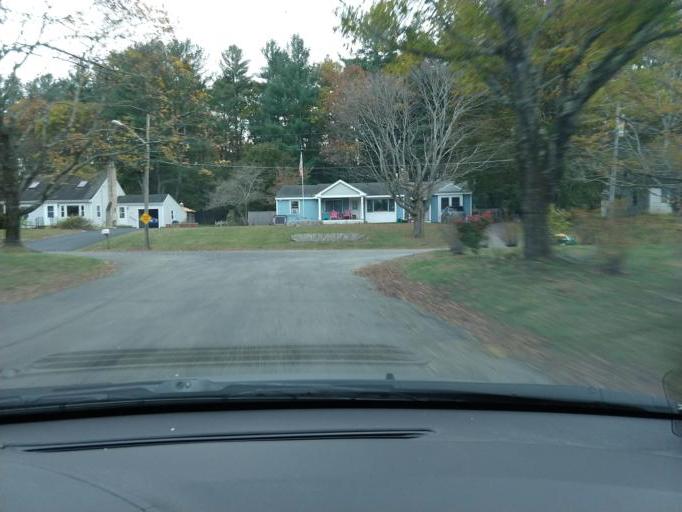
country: US
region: Massachusetts
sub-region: Middlesex County
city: Concord
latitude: 42.4646
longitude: -71.3343
